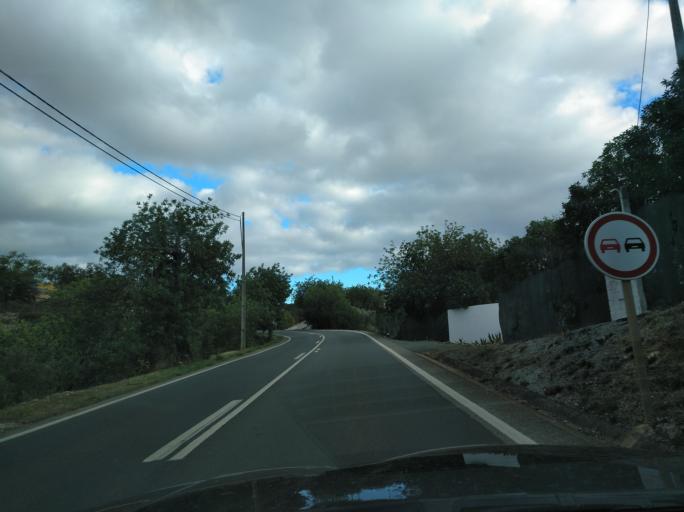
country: PT
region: Faro
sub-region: Tavira
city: Luz
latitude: 37.1434
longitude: -7.7182
